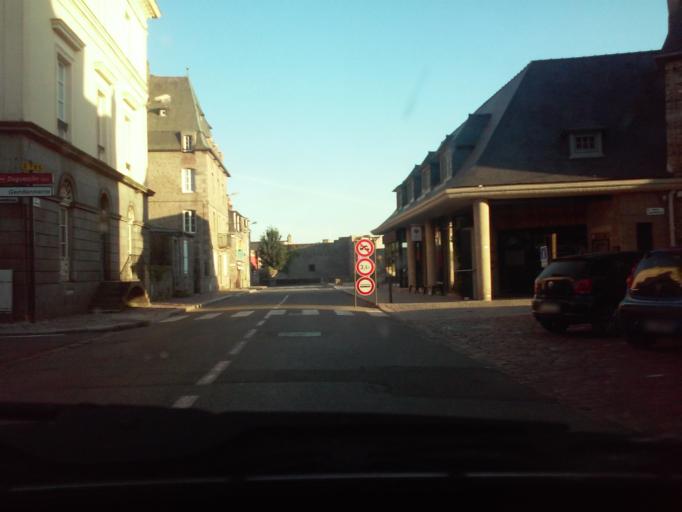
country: FR
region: Brittany
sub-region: Departement des Cotes-d'Armor
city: Lehon
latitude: 48.4510
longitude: -2.0443
